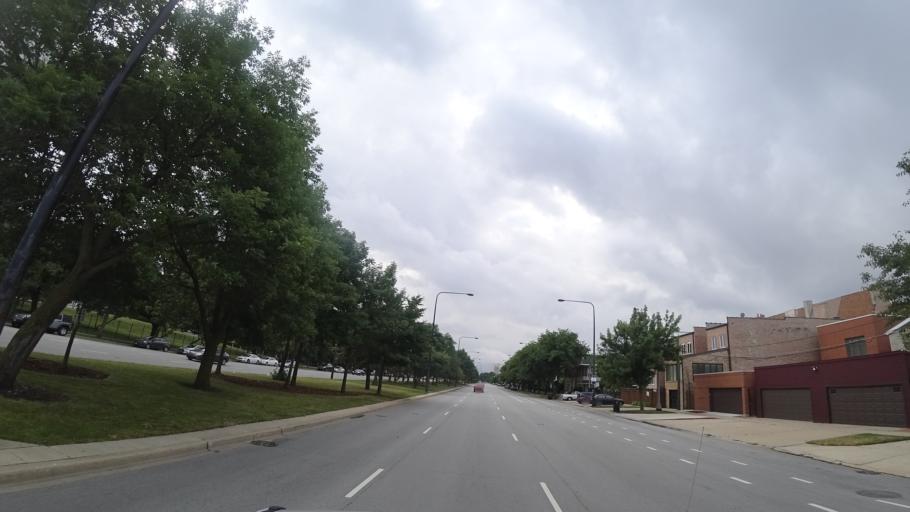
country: US
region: Illinois
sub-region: Cook County
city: Chicago
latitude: 41.8366
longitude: -87.6174
